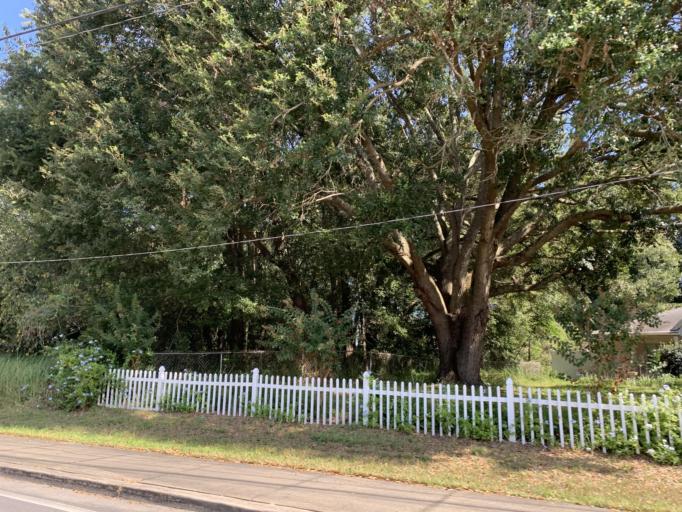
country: US
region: Florida
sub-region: Marion County
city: Silver Springs Shores
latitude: 29.1629
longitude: -82.0668
